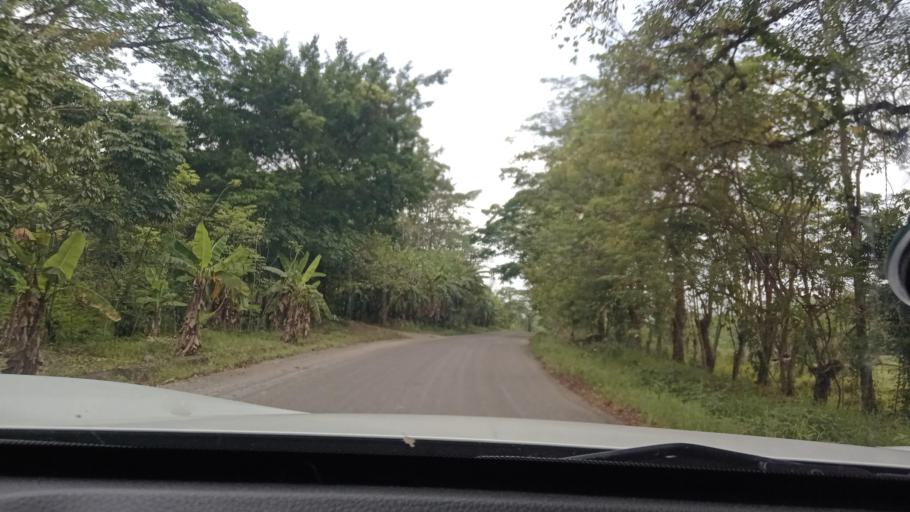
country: MX
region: Tabasco
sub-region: Huimanguillo
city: Francisco Rueda
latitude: 17.5408
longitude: -94.1272
